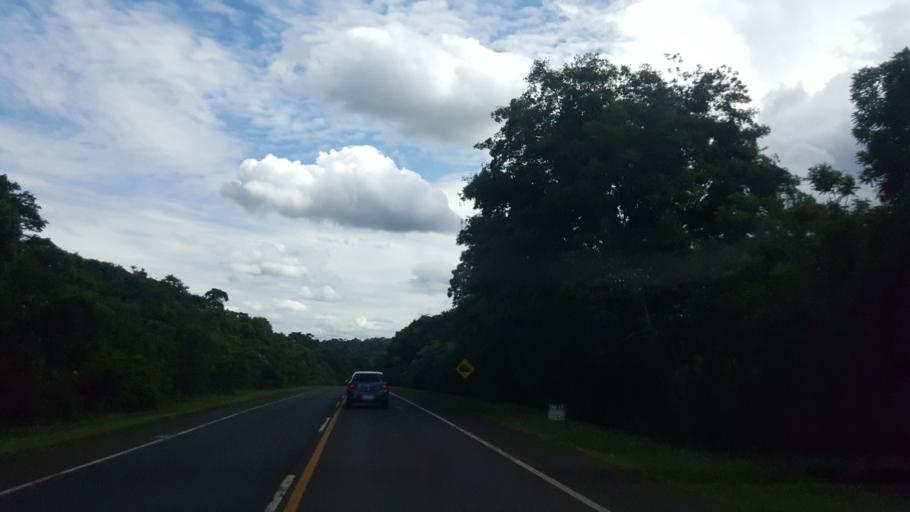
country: AR
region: Misiones
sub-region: Departamento de Iguazu
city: Puerto Iguazu
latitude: -25.7002
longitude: -54.5148
